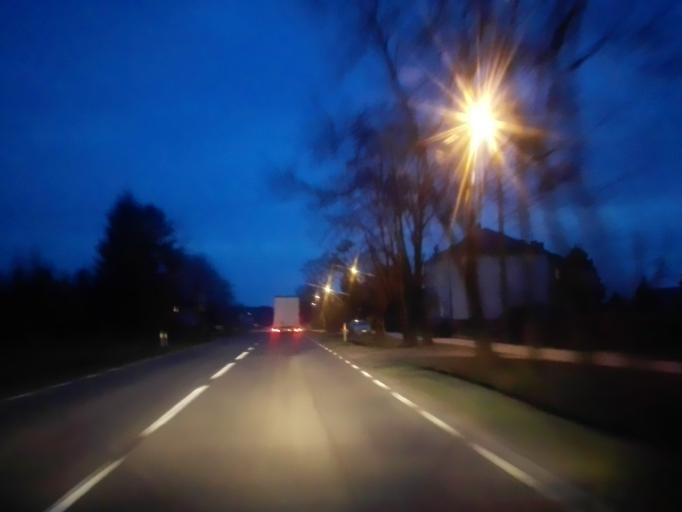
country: PL
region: Podlasie
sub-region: Powiat lomzynski
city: Sniadowo
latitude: 53.0390
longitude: 21.9848
